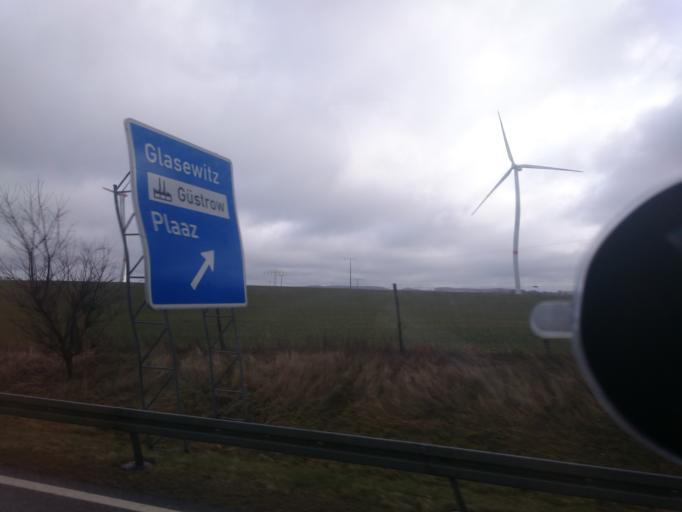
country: DE
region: Mecklenburg-Vorpommern
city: Muhl Rosin
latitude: 53.8229
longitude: 12.3005
